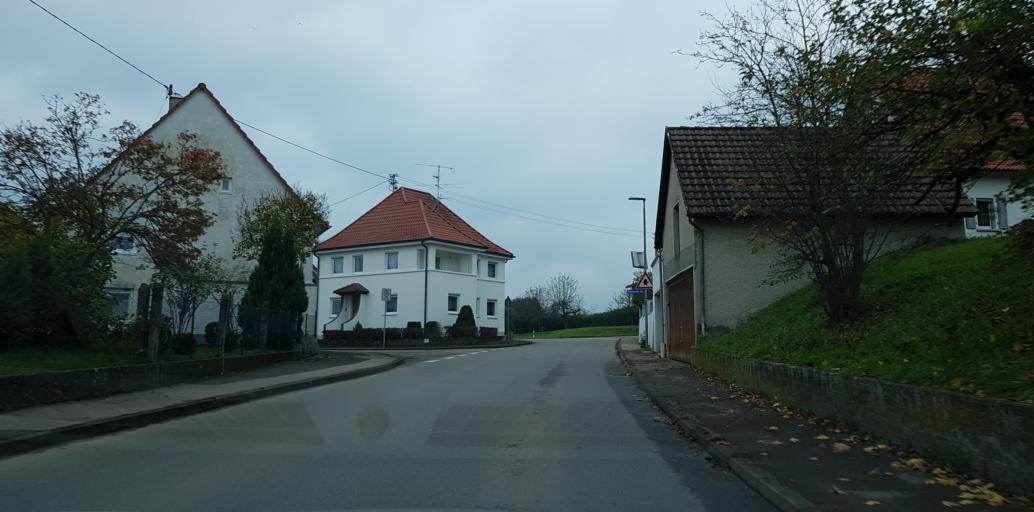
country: DE
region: Baden-Wuerttemberg
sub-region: Tuebingen Region
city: Oberdischingen
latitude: 48.3038
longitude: 9.8279
